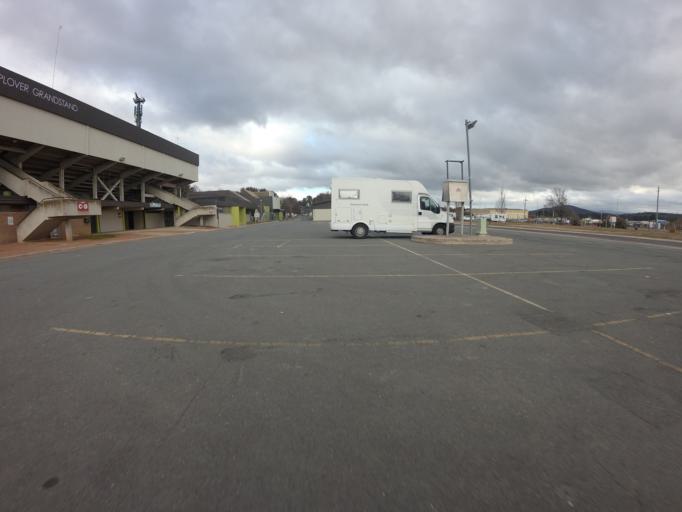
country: AU
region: Australian Capital Territory
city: Kaleen
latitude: -35.2305
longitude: 149.1458
